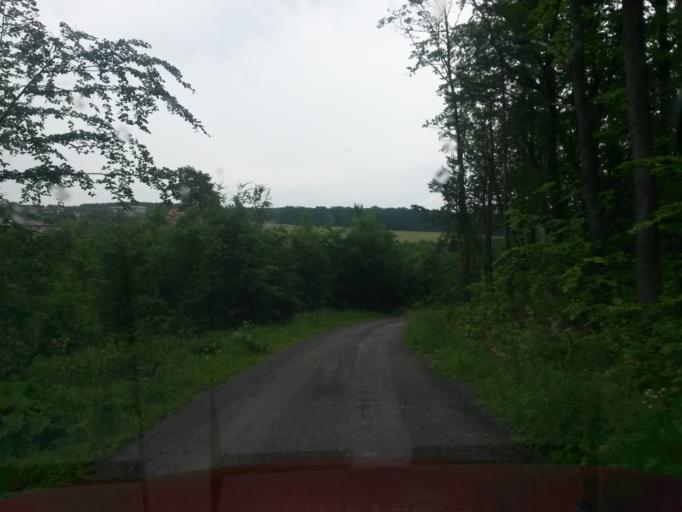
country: SK
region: Kosicky
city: Kosice
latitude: 48.7034
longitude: 21.1852
